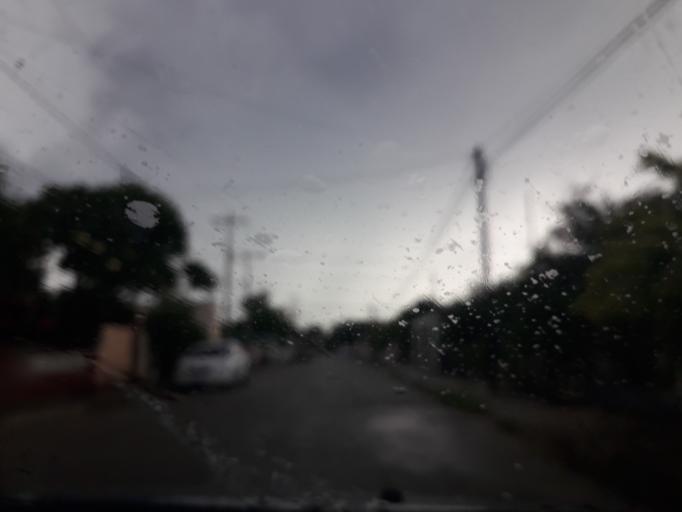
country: MX
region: Yucatan
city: Merida
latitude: 20.9794
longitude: -89.6528
